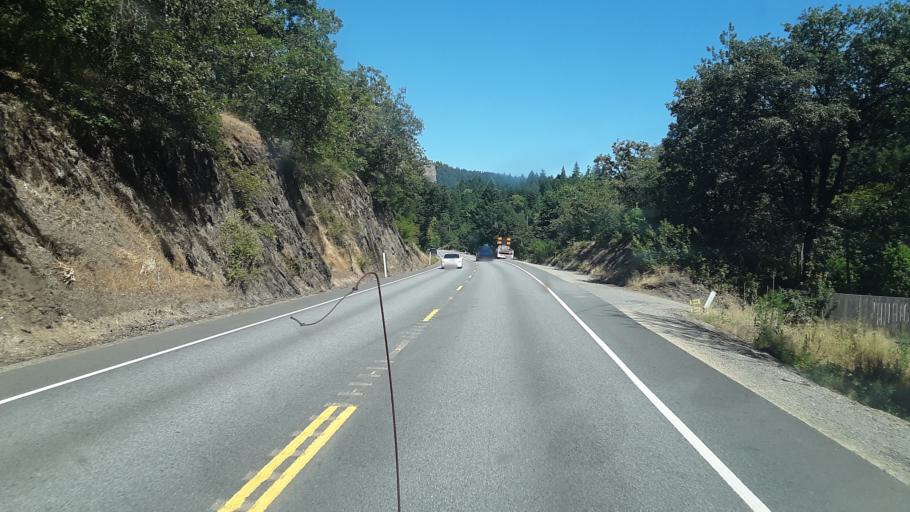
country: US
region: Oregon
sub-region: Josephine County
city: Redwood
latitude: 42.3627
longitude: -123.5235
